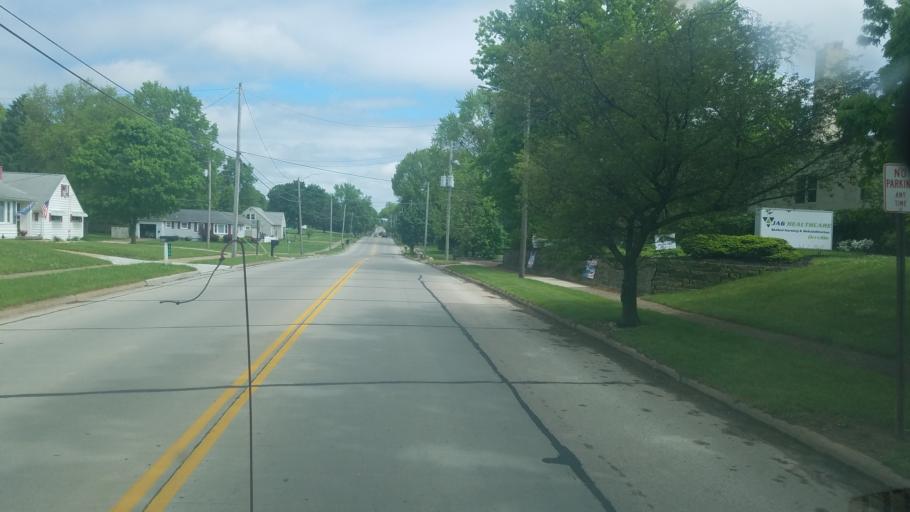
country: US
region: Ohio
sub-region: Wayne County
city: Orrville
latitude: 40.8373
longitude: -81.7844
